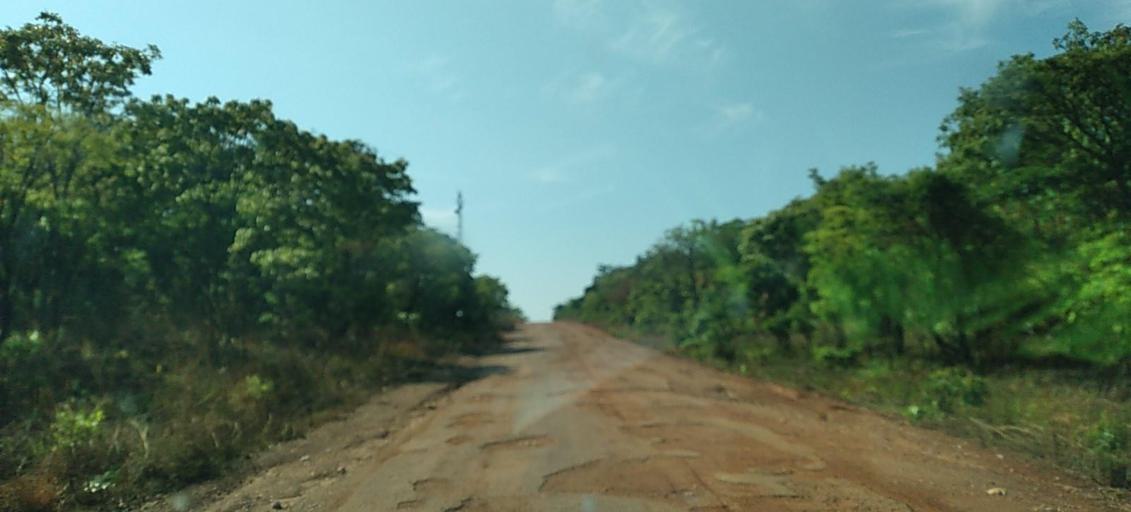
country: ZM
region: North-Western
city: Mwinilunga
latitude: -11.8082
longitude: 25.0824
